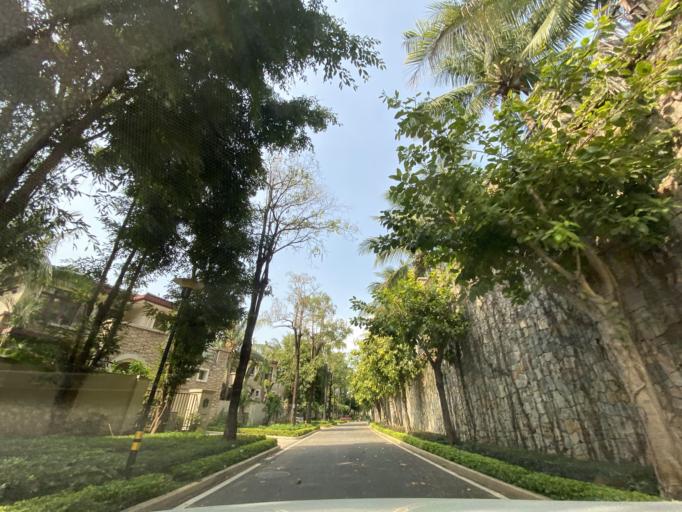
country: CN
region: Hainan
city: Yingzhou
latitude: 18.4098
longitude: 109.8432
